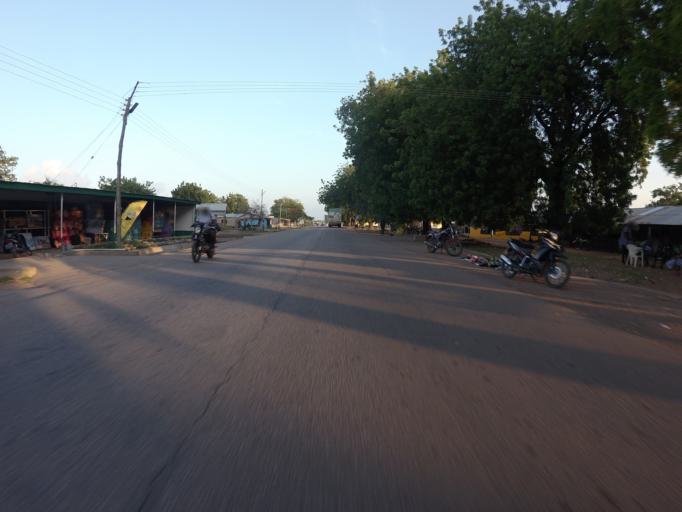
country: GH
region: Upper East
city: Navrongo
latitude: 10.9682
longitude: -1.1018
